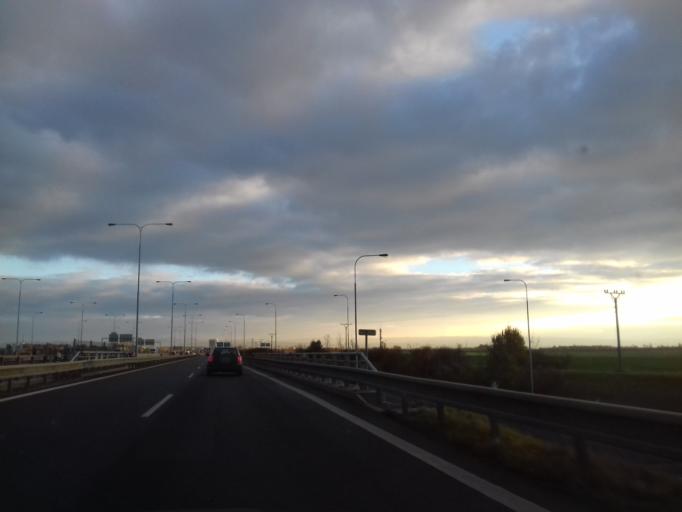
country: CZ
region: Olomoucky
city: Hnevotin
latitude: 49.5631
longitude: 17.2020
